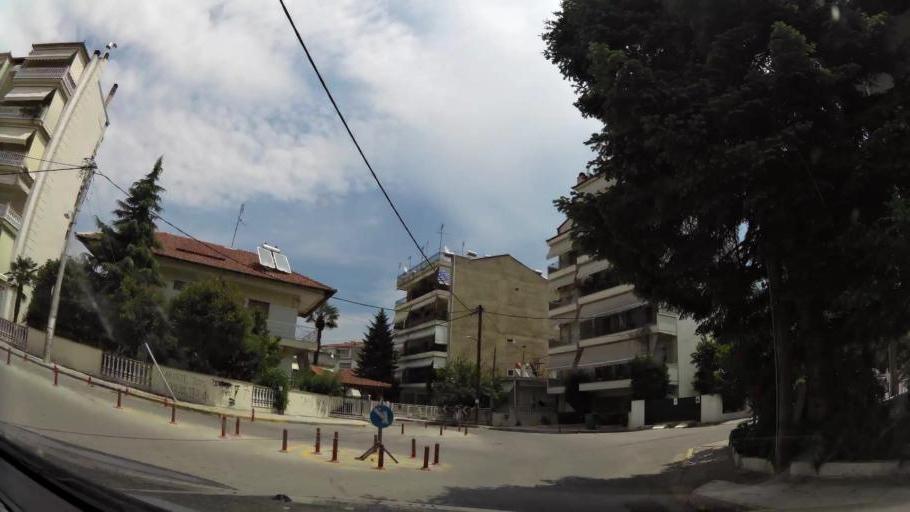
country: GR
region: Central Macedonia
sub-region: Nomos Pierias
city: Katerini
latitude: 40.2675
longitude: 22.5120
